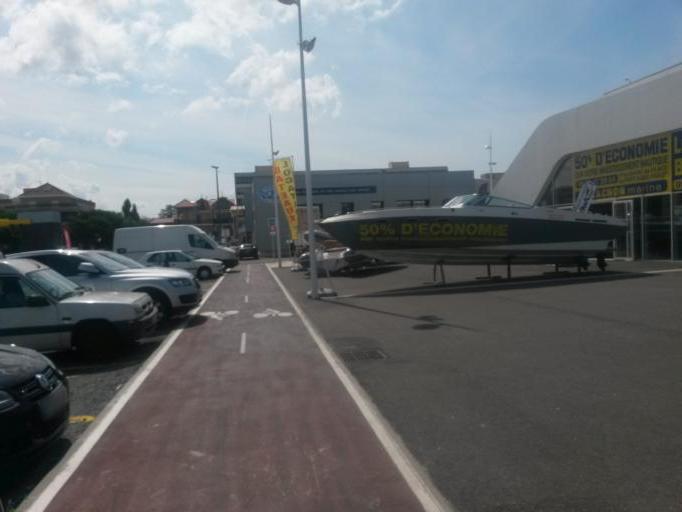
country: FR
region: Aquitaine
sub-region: Departement de la Gironde
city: Arcachon
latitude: 44.6575
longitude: -1.1437
